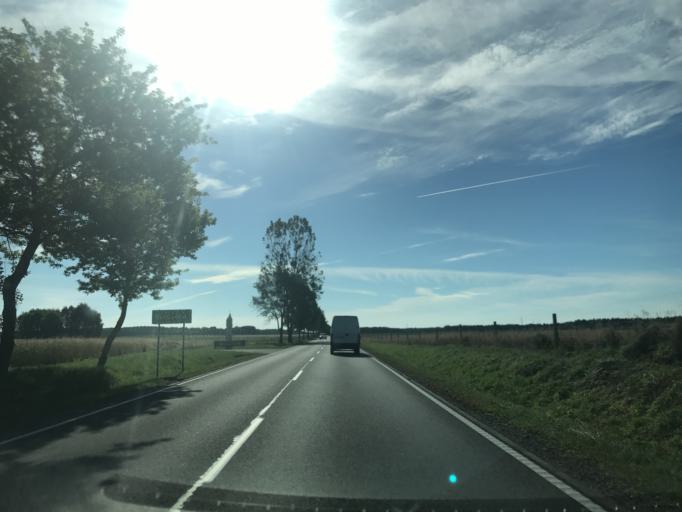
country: PL
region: Pomeranian Voivodeship
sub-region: Powiat czluchowski
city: Rzeczenica
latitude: 53.7544
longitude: 17.1278
